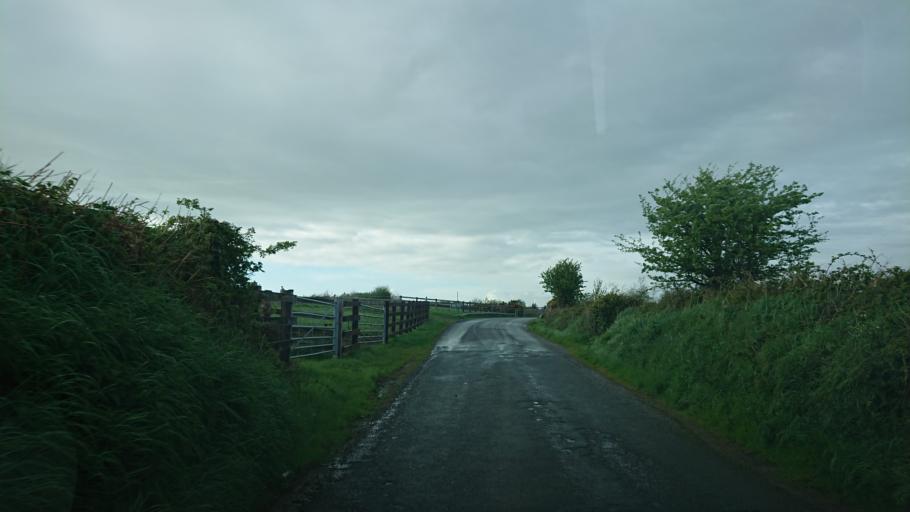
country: IE
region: Munster
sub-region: Waterford
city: Waterford
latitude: 52.2237
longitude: -7.1318
